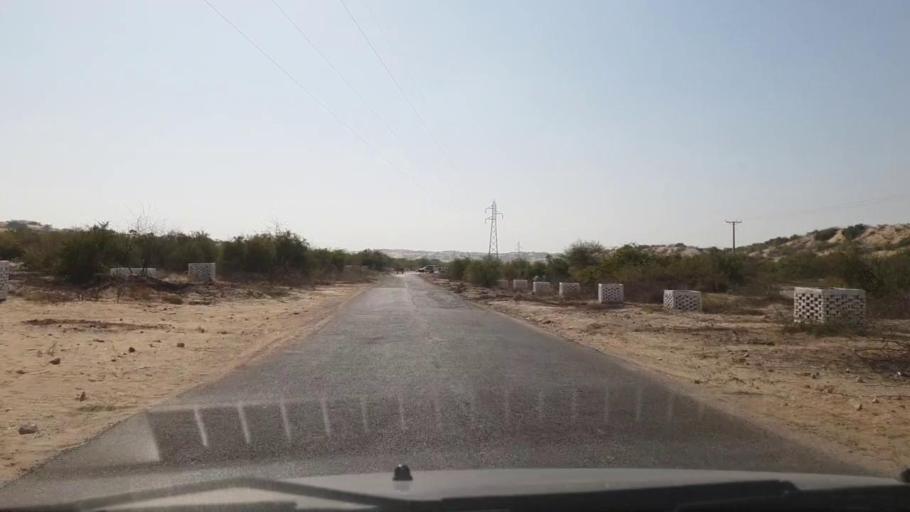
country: PK
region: Sindh
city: Diplo
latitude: 24.4885
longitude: 69.5894
